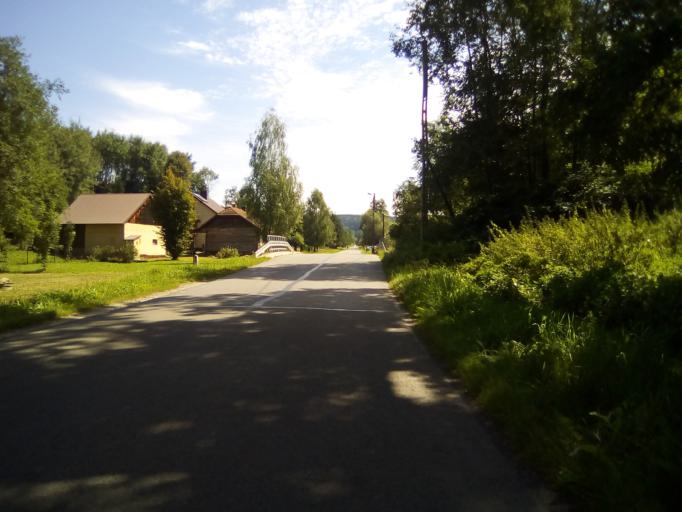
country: PL
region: Subcarpathian Voivodeship
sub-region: Powiat strzyzowski
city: Konieczkowa
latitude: 49.8395
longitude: 21.9285
